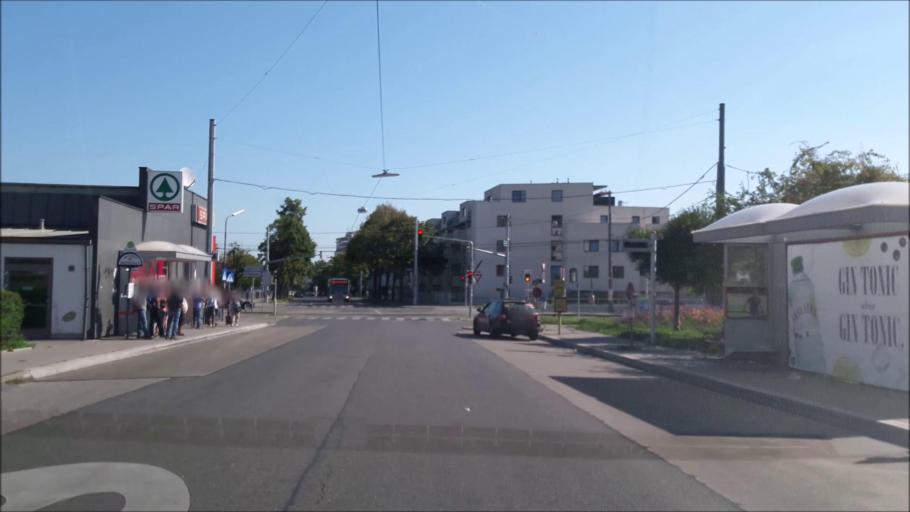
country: AT
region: Lower Austria
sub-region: Politischer Bezirk Wien-Umgebung
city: Schwechat
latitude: 48.1617
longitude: 16.4283
